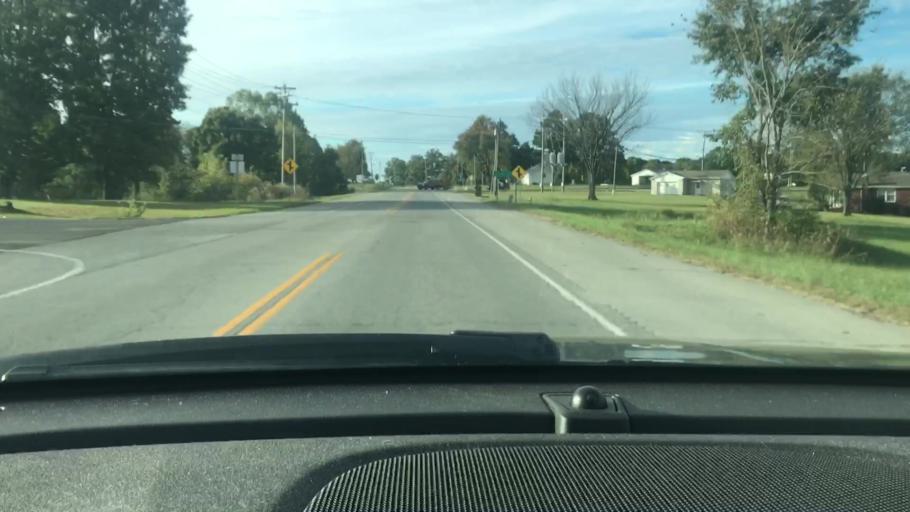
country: US
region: Tennessee
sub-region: Dickson County
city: White Bluff
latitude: 36.1364
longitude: -87.2383
